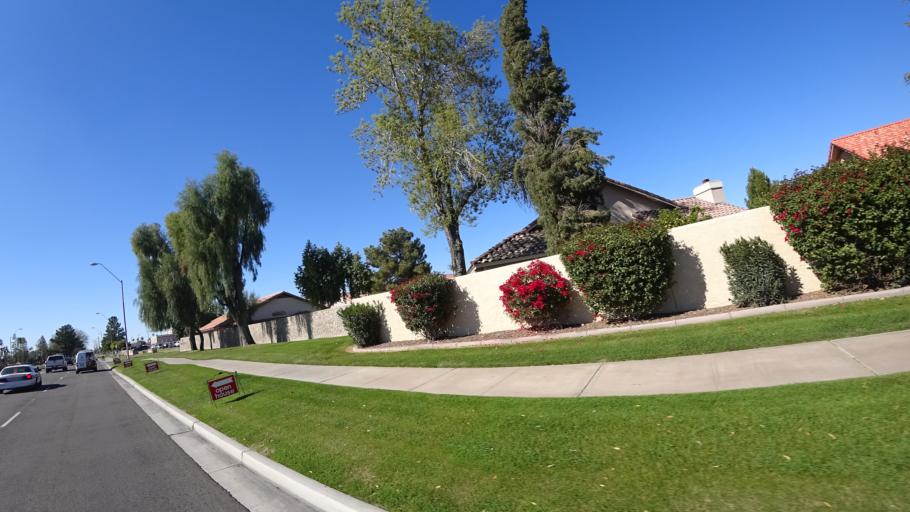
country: US
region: Arizona
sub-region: Maricopa County
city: Peoria
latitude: 33.6528
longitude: -112.2150
